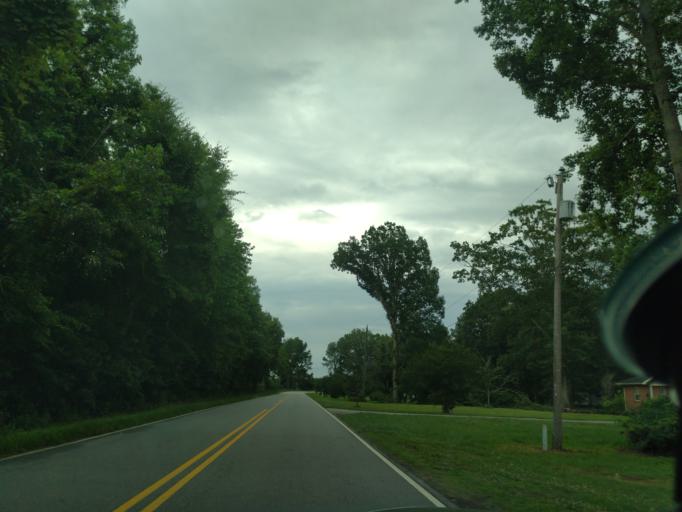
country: US
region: North Carolina
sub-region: Washington County
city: Plymouth
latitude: 35.8773
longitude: -76.6028
